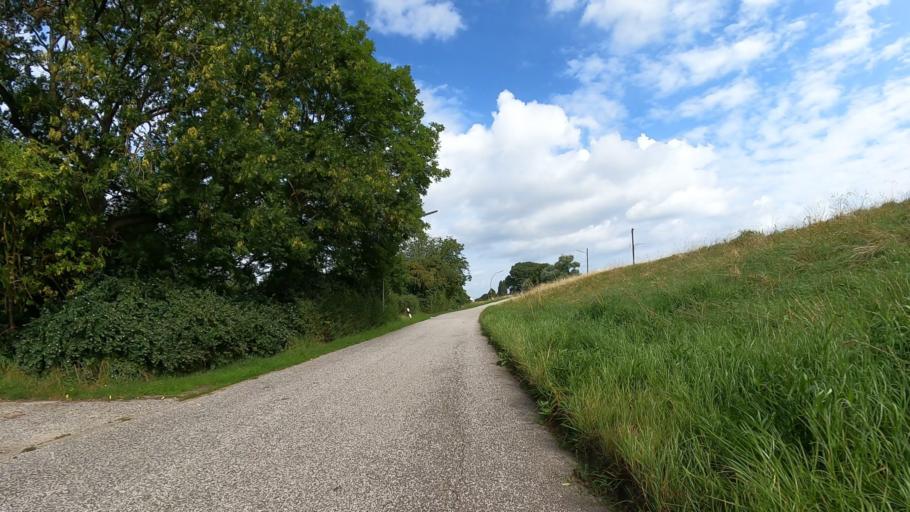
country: DE
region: Lower Saxony
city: Neu Wulmstorf
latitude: 53.5203
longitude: 9.8452
